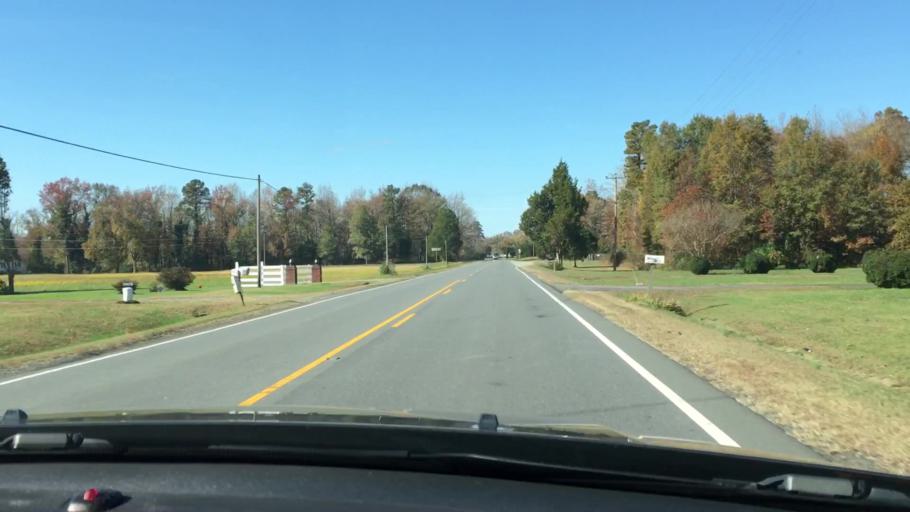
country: US
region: Virginia
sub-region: King William County
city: King William
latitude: 37.6817
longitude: -77.0076
